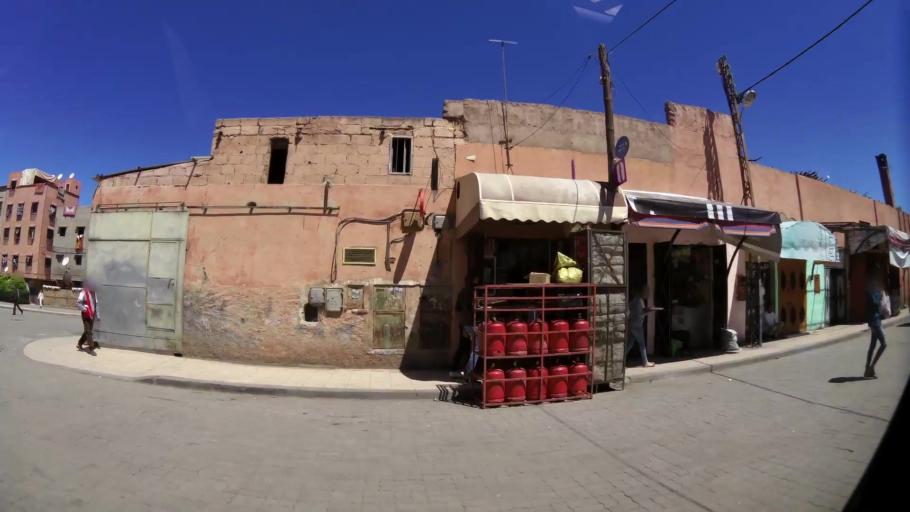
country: MA
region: Marrakech-Tensift-Al Haouz
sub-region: Marrakech
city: Marrakesh
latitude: 31.6550
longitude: -7.9920
